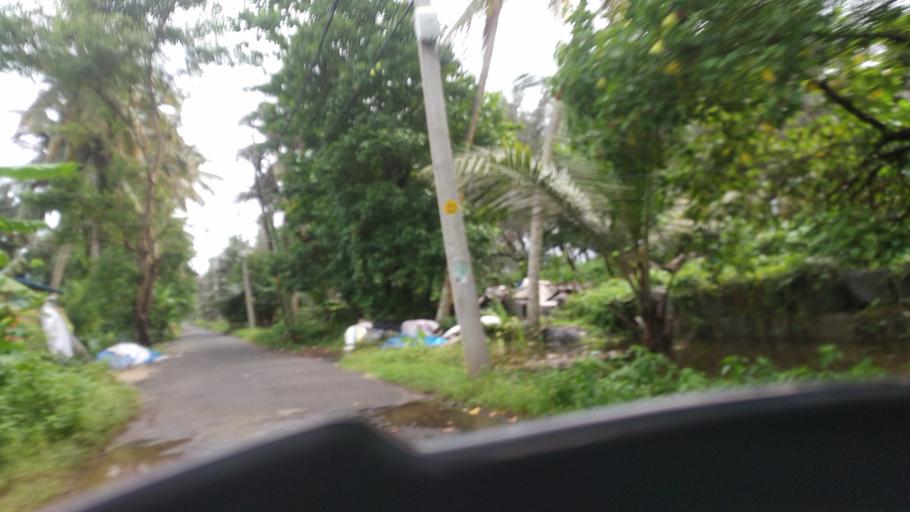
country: IN
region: Kerala
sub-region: Ernakulam
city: Elur
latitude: 10.1144
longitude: 76.1867
